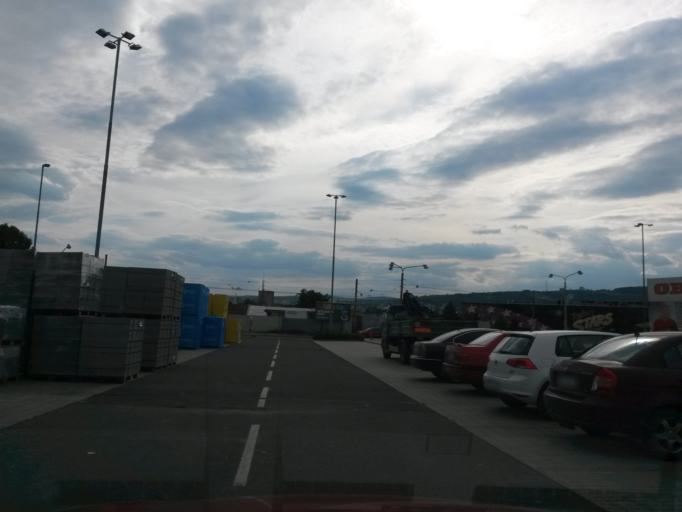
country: SK
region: Kosicky
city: Kosice
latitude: 48.7395
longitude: 21.2695
